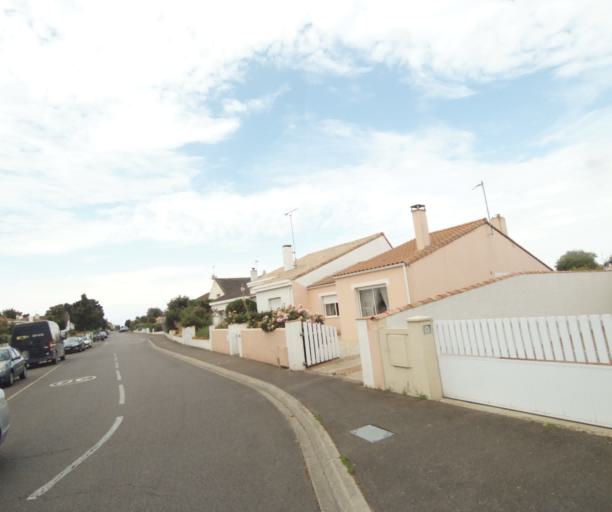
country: FR
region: Pays de la Loire
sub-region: Departement de la Vendee
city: Chateau-d'Olonne
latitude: 46.4983
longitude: -1.7571
